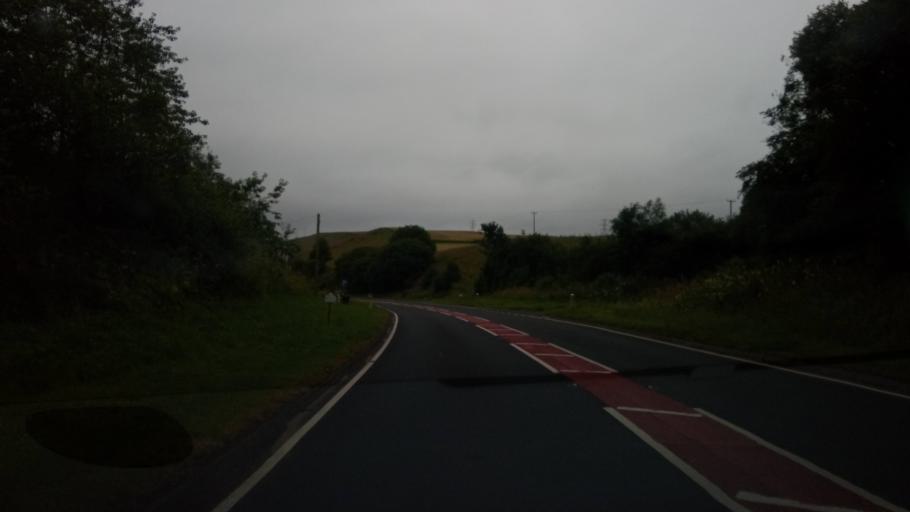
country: GB
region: Scotland
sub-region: The Scottish Borders
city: Hawick
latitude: 55.3838
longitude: -2.8682
